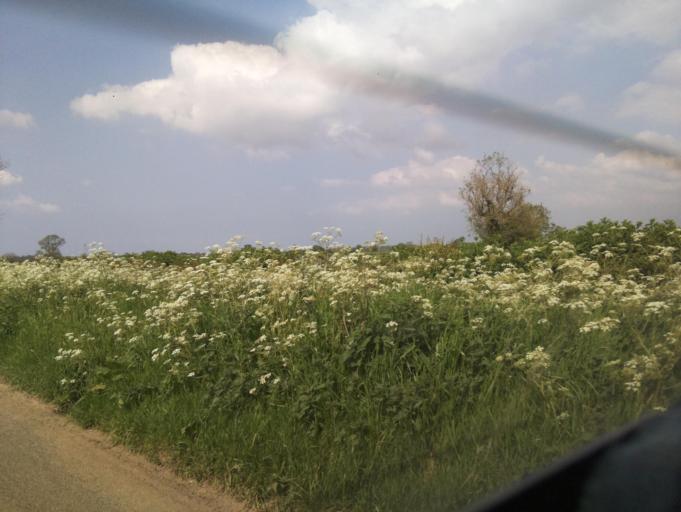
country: GB
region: England
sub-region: Wiltshire
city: Luckington
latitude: 51.5812
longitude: -2.2208
